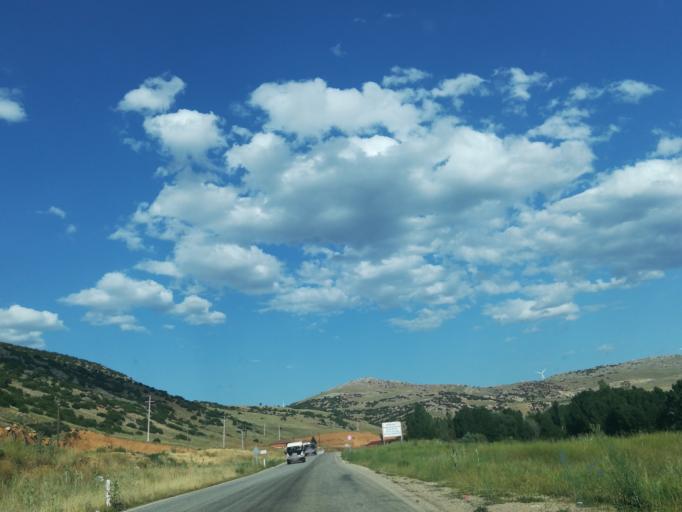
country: TR
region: Afyonkarahisar
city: Dinar
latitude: 38.0994
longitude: 30.1519
